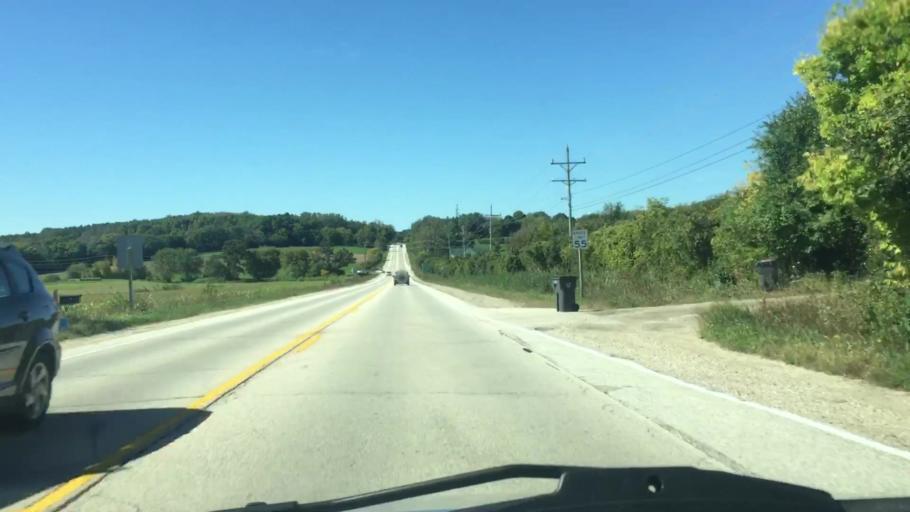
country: US
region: Wisconsin
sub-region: Waukesha County
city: Pewaukee
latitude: 43.0210
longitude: -88.3046
